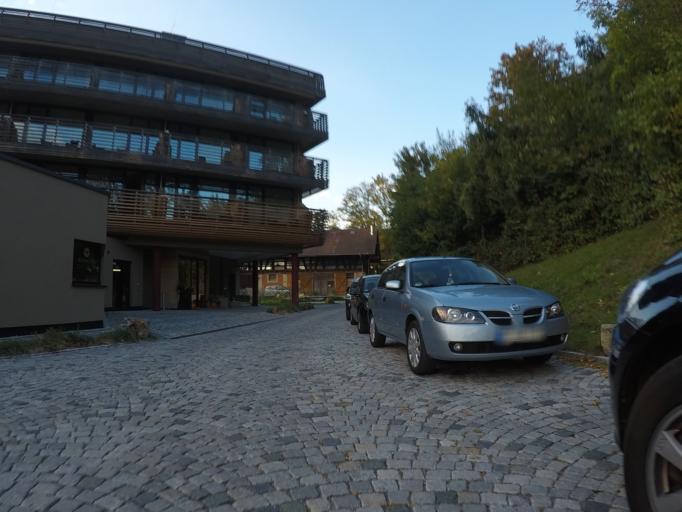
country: DE
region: Baden-Wuerttemberg
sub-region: Tuebingen Region
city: Eningen unter Achalm
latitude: 48.4910
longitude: 9.2403
